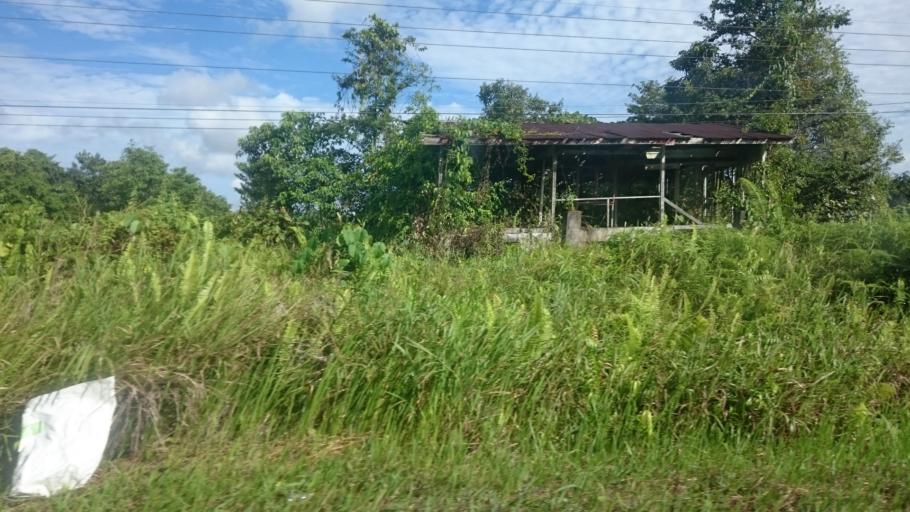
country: MY
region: Sarawak
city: Limbang
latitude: 4.6545
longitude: 114.9671
